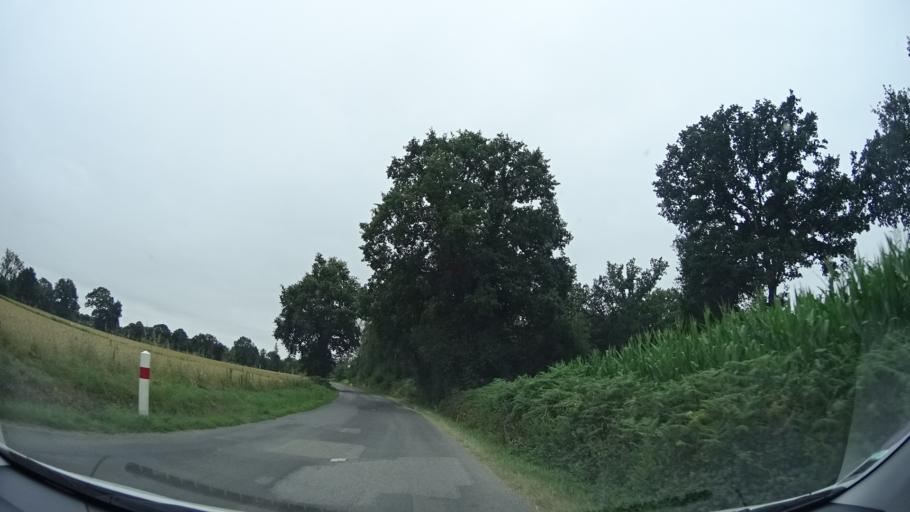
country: FR
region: Brittany
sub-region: Departement d'Ille-et-Vilaine
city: Hede-Bazouges
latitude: 48.2846
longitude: -1.7734
